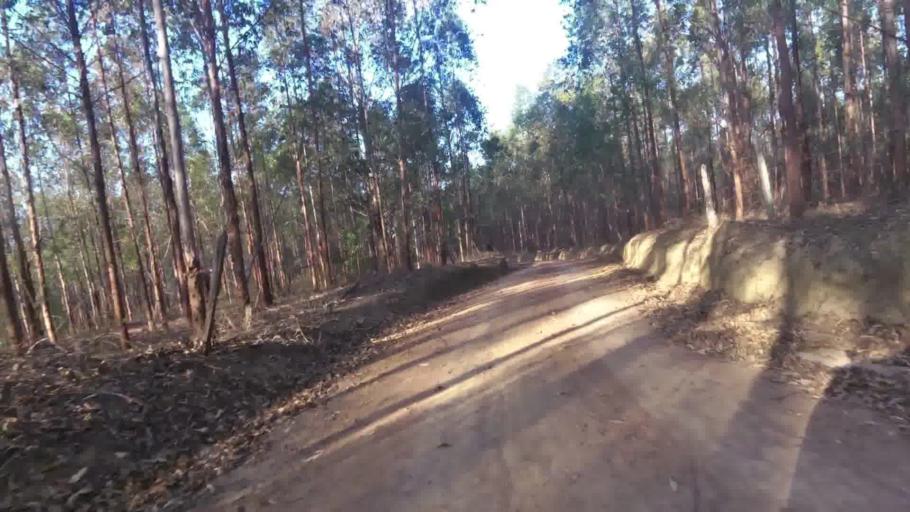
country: BR
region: Espirito Santo
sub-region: Marataizes
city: Marataizes
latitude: -21.1630
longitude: -41.0413
